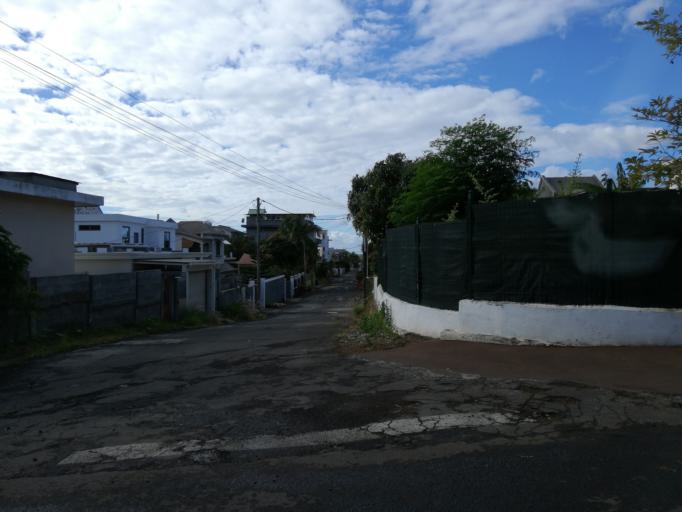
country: MU
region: Black River
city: Petite Riviere
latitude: -20.2015
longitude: 57.4659
